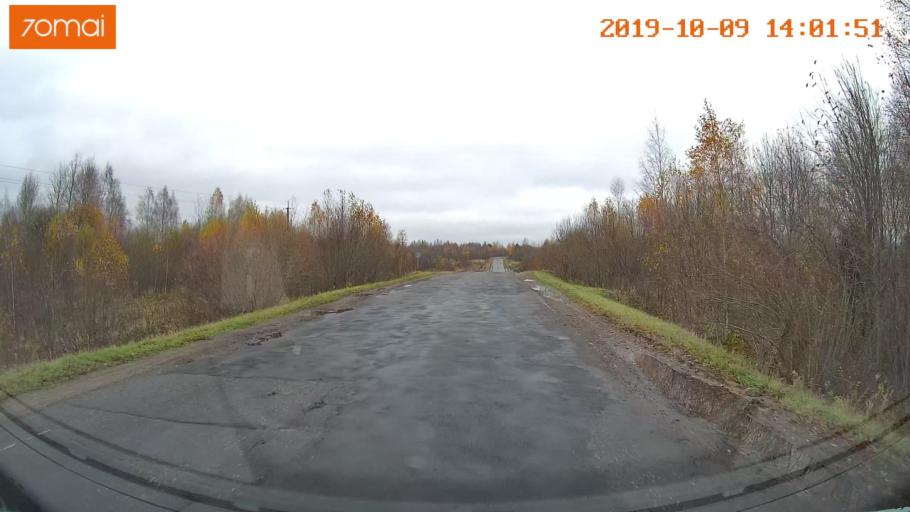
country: RU
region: Kostroma
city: Buy
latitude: 58.4460
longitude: 41.3507
